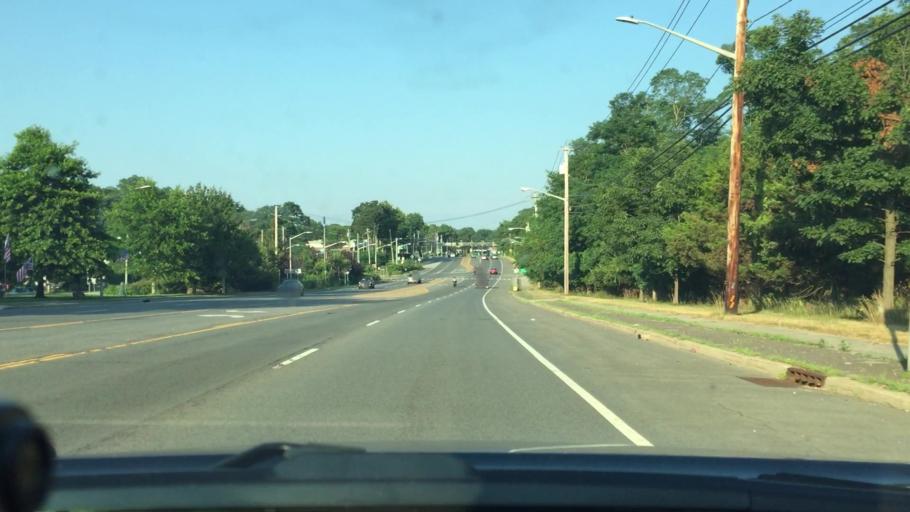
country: US
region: New York
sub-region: Suffolk County
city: Sound Beach
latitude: 40.9446
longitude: -72.9642
